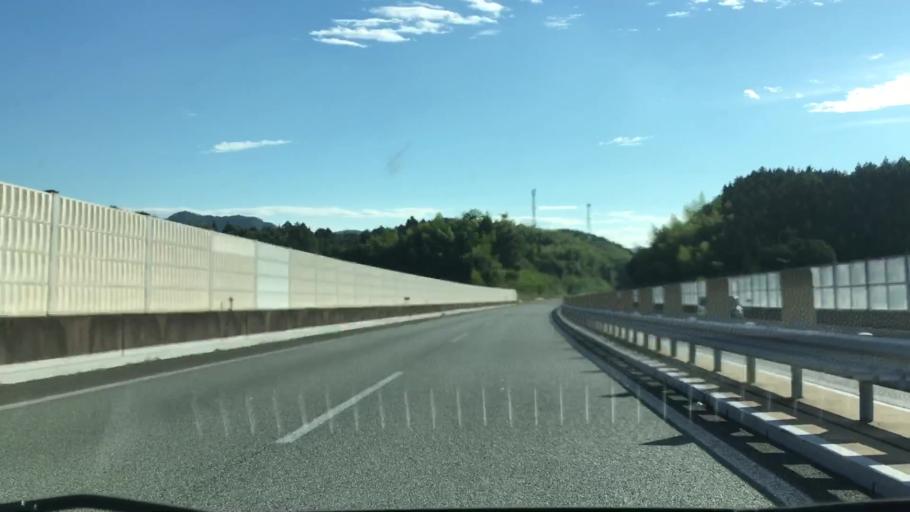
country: JP
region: Yamaguchi
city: Yanai
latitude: 34.0878
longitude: 132.0921
